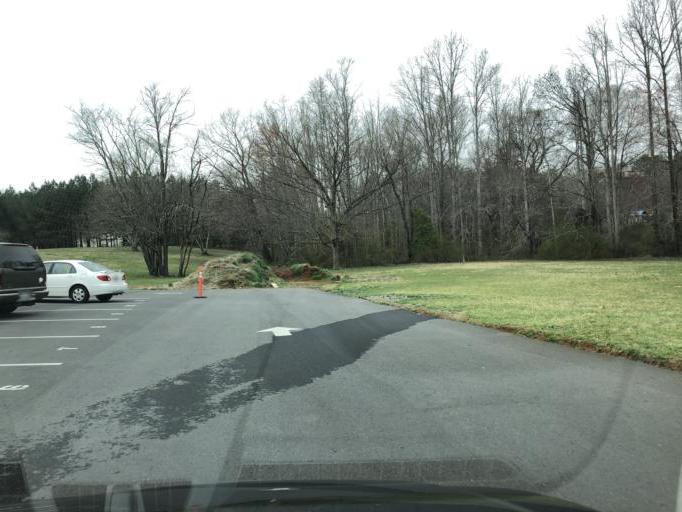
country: US
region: North Carolina
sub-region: Cleveland County
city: Shelby
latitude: 35.2611
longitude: -81.5036
